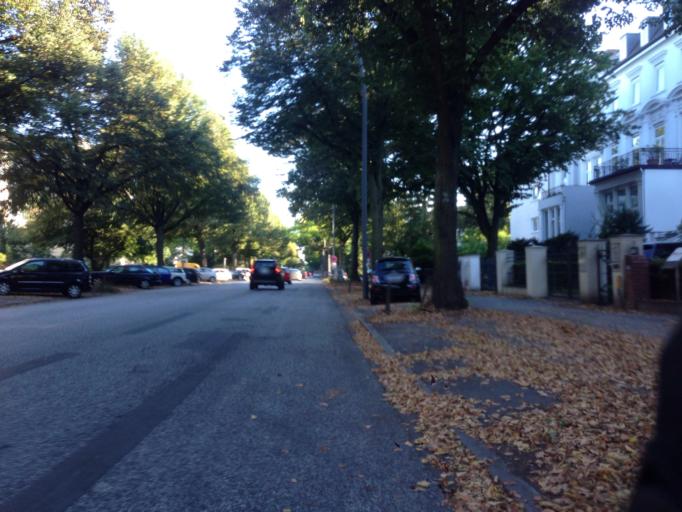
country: DE
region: Hamburg
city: Eimsbuettel
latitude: 53.5765
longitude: 9.9888
